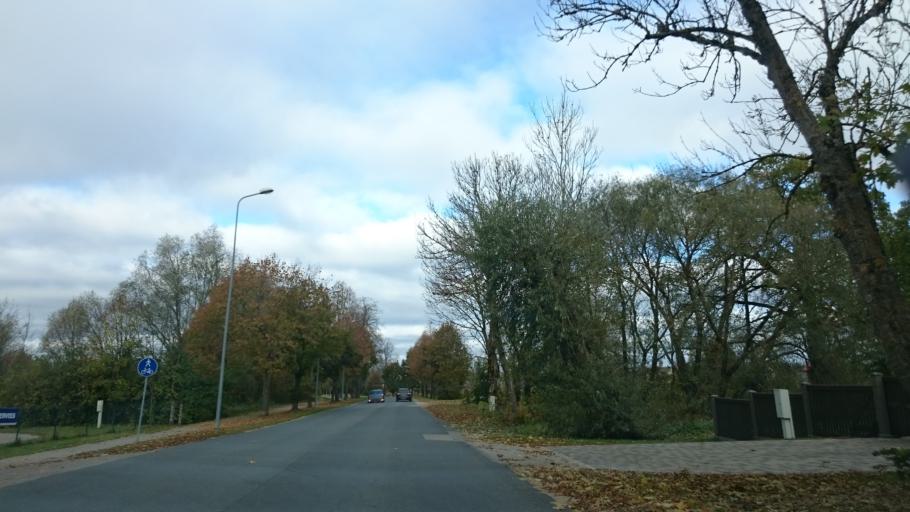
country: LV
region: Cesu Rajons
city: Cesis
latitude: 57.3002
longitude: 25.2692
